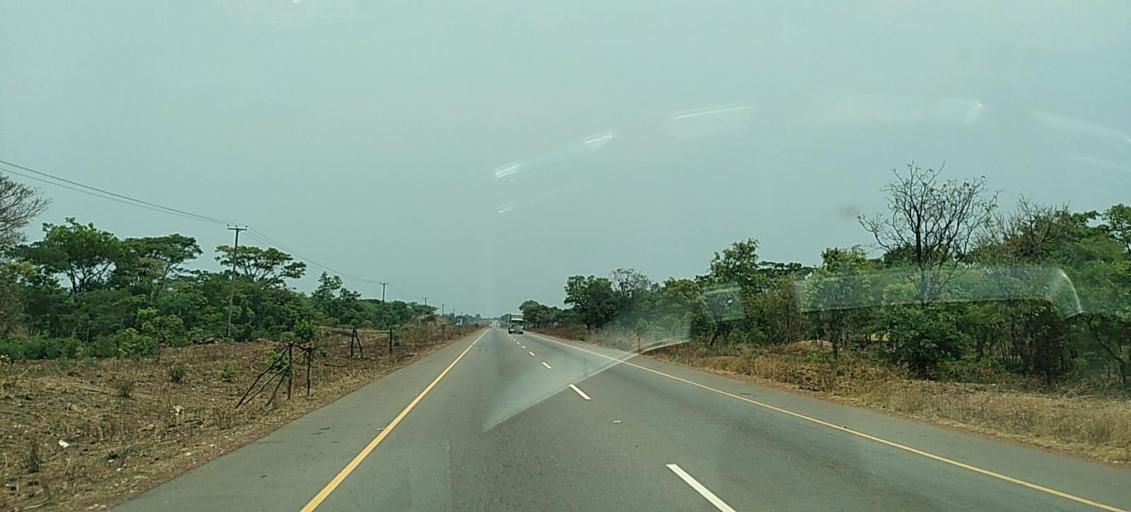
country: ZM
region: Copperbelt
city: Chililabombwe
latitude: -12.4408
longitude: 27.4186
